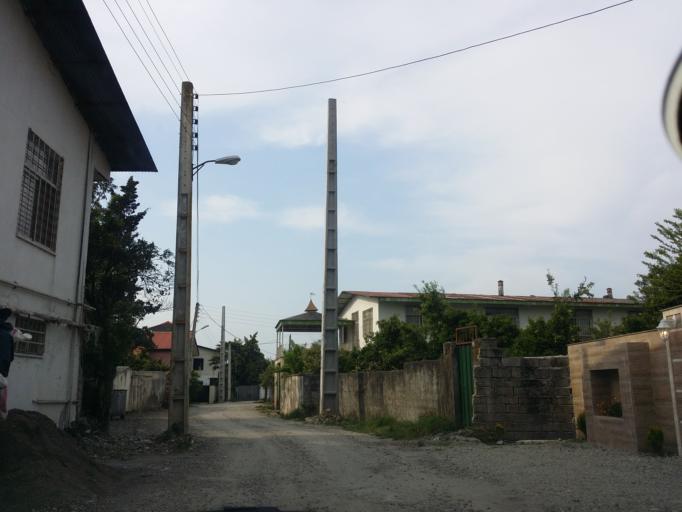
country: IR
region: Mazandaran
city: Chalus
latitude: 36.6794
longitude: 51.3931
